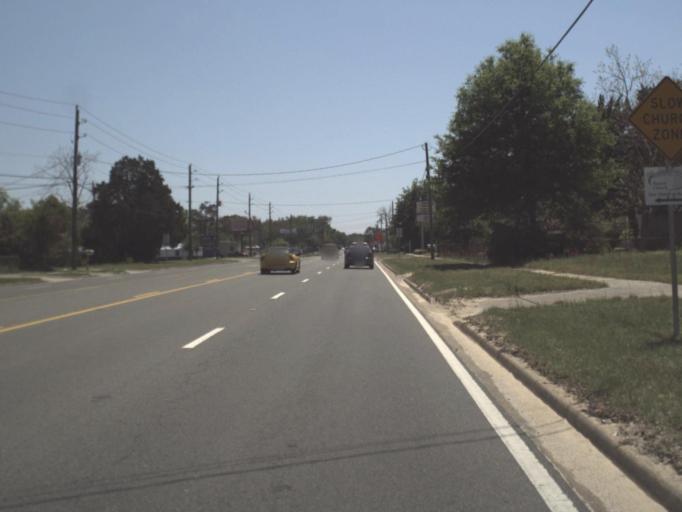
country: US
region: Florida
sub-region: Escambia County
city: Bellview
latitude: 30.4820
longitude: -87.3067
